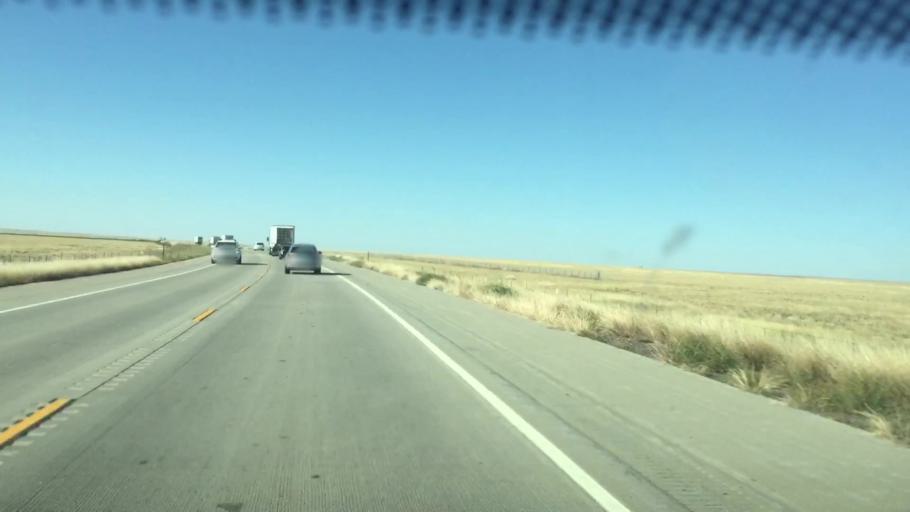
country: US
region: Colorado
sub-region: Kiowa County
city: Eads
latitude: 38.3544
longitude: -102.7158
